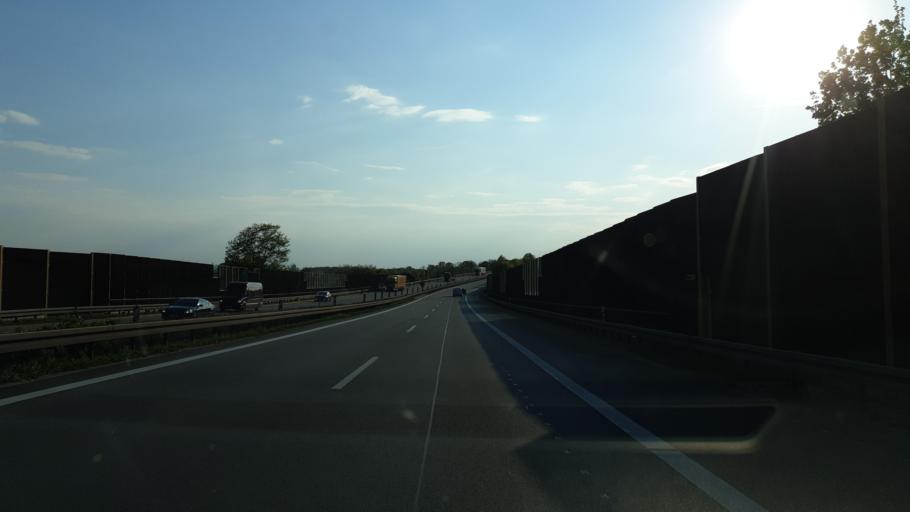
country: DE
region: Saxony
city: Bautzen
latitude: 51.1868
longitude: 14.4057
